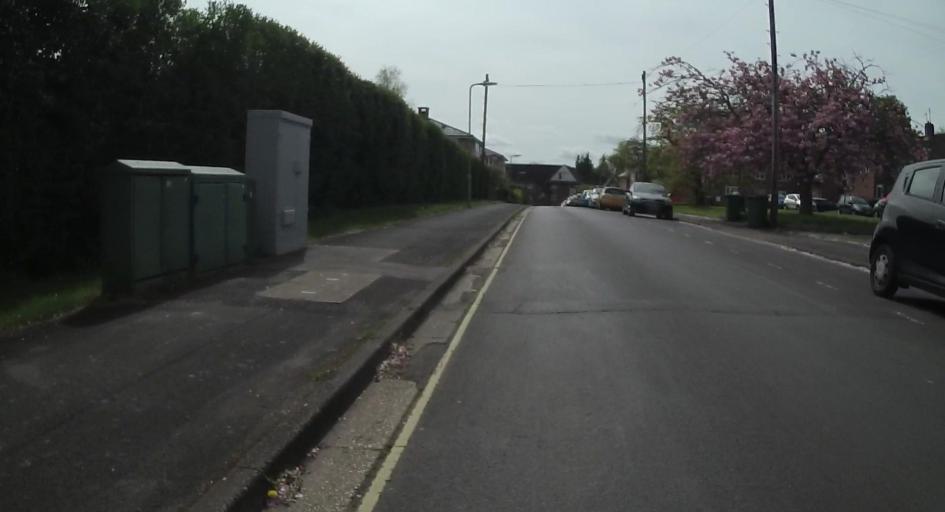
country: GB
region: England
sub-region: Hampshire
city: Winchester
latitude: 51.0628
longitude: -1.3357
